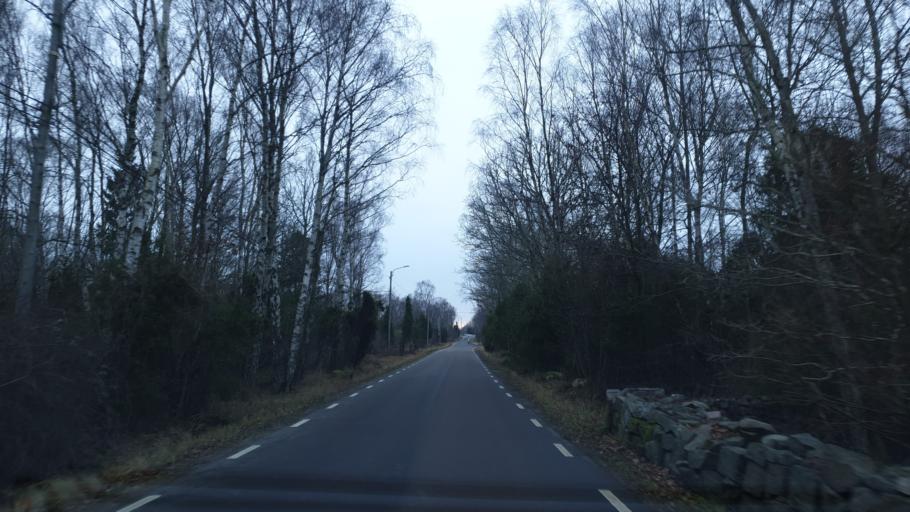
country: SE
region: Blekinge
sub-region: Karlskrona Kommun
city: Karlskrona
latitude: 56.1158
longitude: 15.6147
